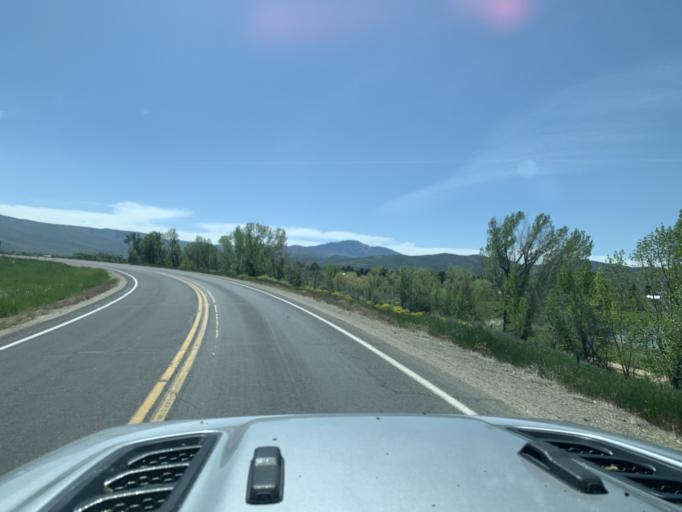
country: US
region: Utah
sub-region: Weber County
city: Wolf Creek
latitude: 41.2682
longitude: -111.7761
